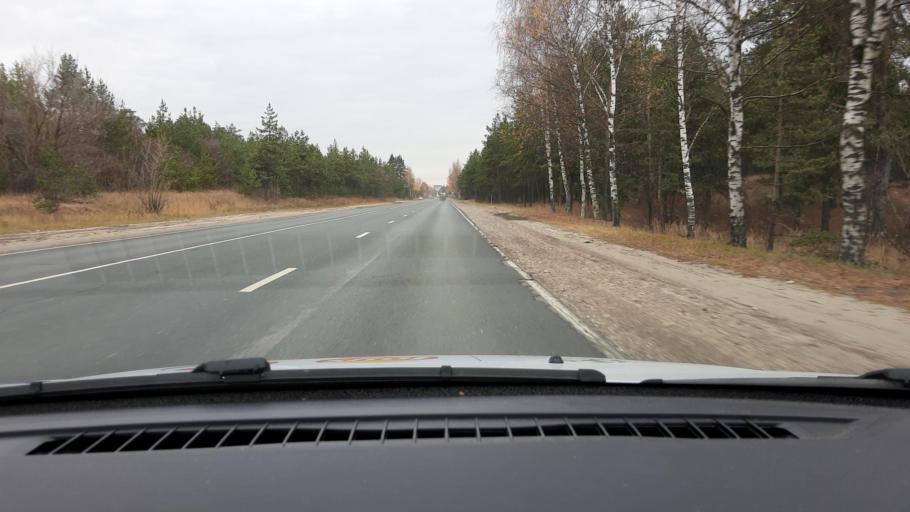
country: RU
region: Nizjnij Novgorod
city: Dzerzhinsk
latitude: 56.2726
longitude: 43.4738
